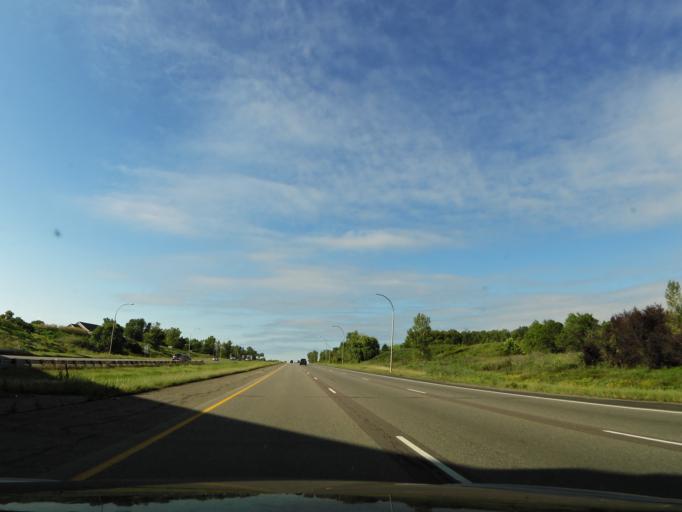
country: US
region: Minnesota
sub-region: Dakota County
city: Inver Grove Heights
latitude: 44.8729
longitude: -93.0808
